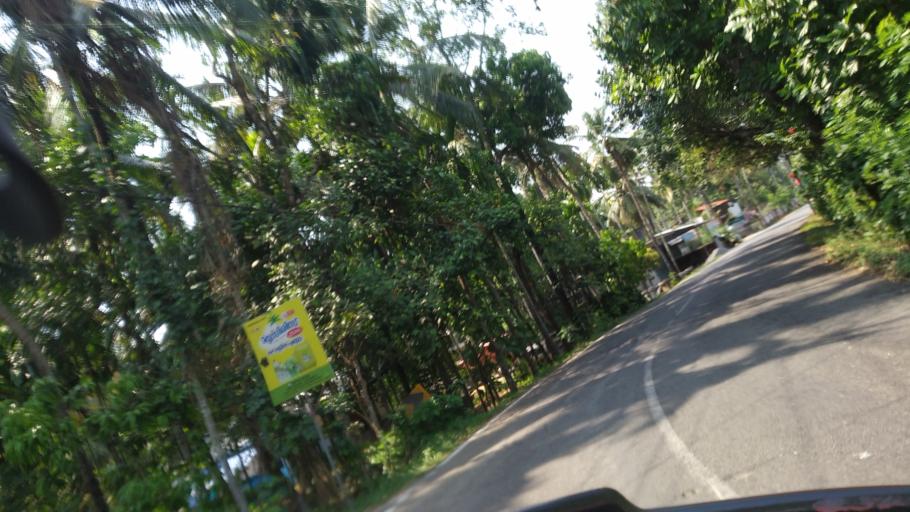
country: IN
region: Kerala
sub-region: Thrissur District
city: Irinjalakuda
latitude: 10.2911
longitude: 76.1346
